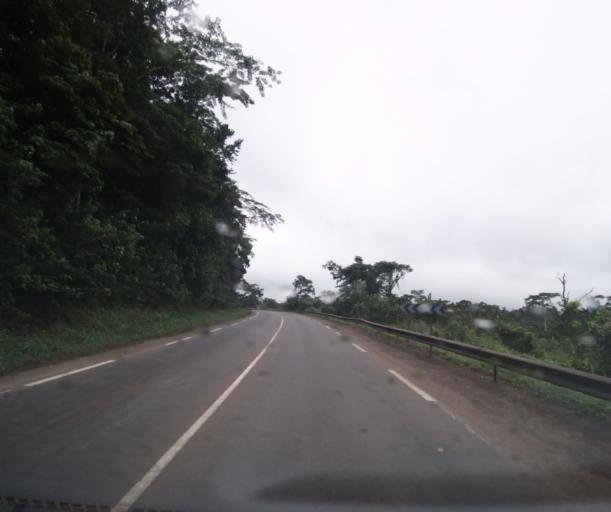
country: CM
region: Centre
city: Mbankomo
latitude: 3.7738
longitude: 11.1519
